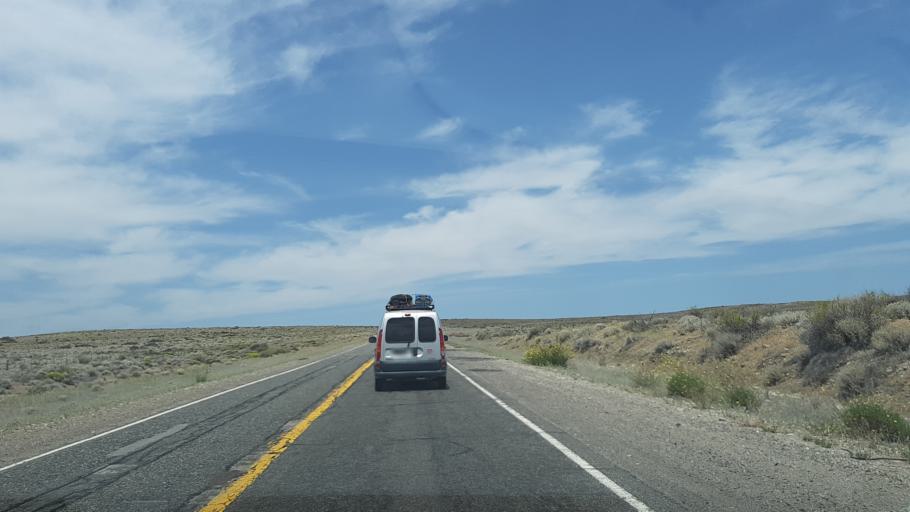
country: AR
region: Rio Negro
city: Pilcaniyeu
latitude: -40.4914
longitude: -70.6792
